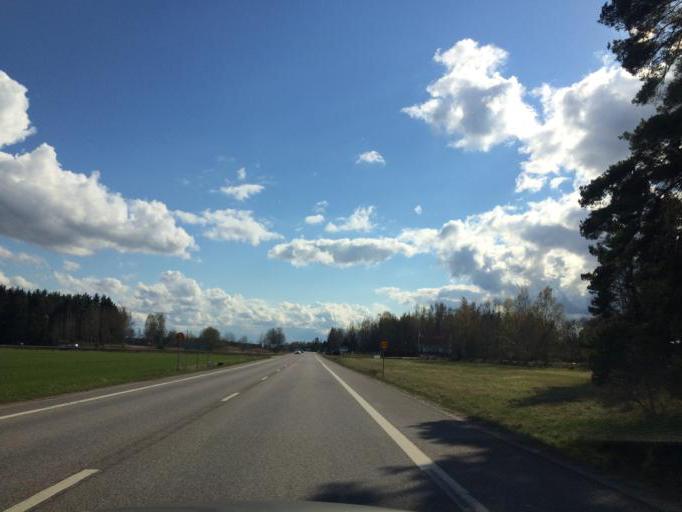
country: SE
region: Soedermanland
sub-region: Eskilstuna Kommun
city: Eskilstuna
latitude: 59.4135
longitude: 16.5846
